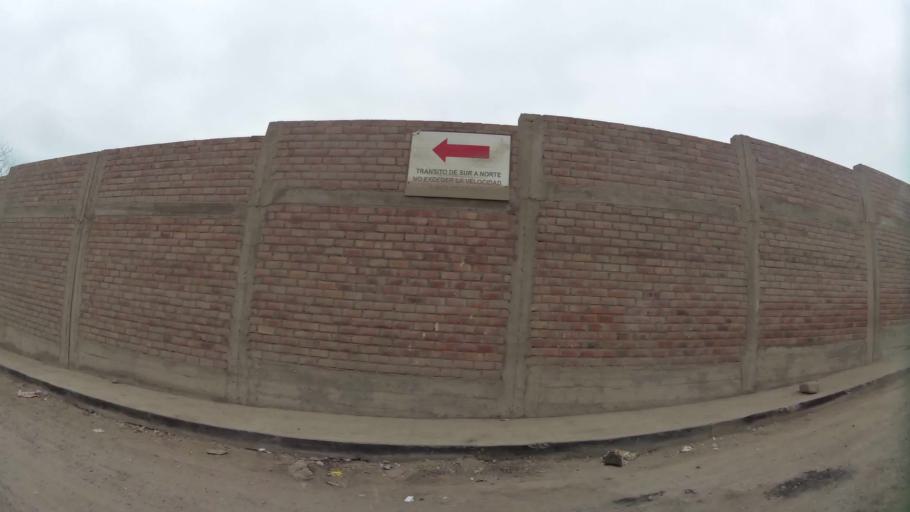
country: PE
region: Lima
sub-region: Lima
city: Surco
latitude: -12.2015
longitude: -76.9712
